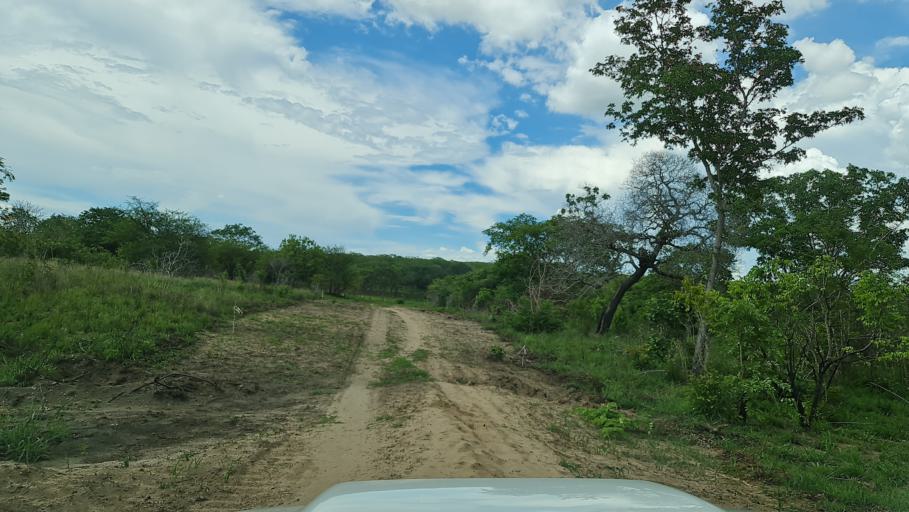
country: MZ
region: Nampula
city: Ilha de Mocambique
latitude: -15.5094
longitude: 40.1915
